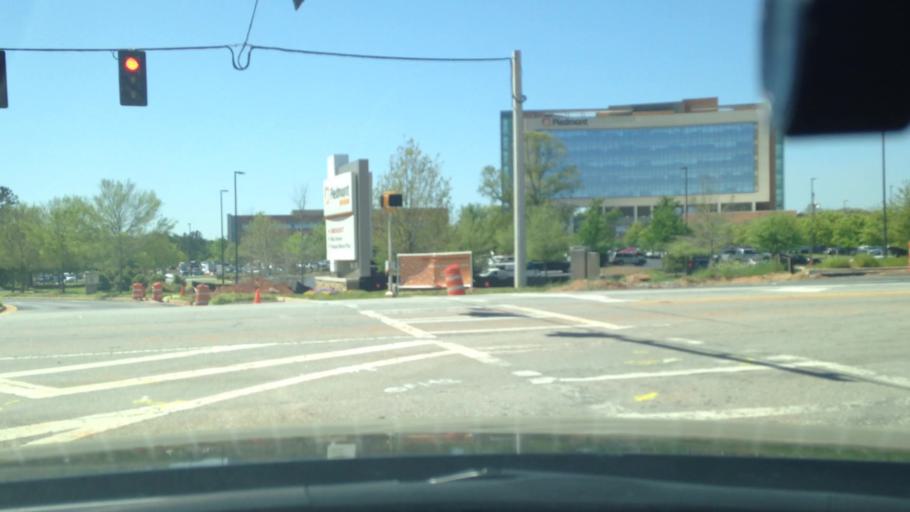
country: US
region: Georgia
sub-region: Coweta County
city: East Newnan
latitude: 33.3594
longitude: -84.7532
